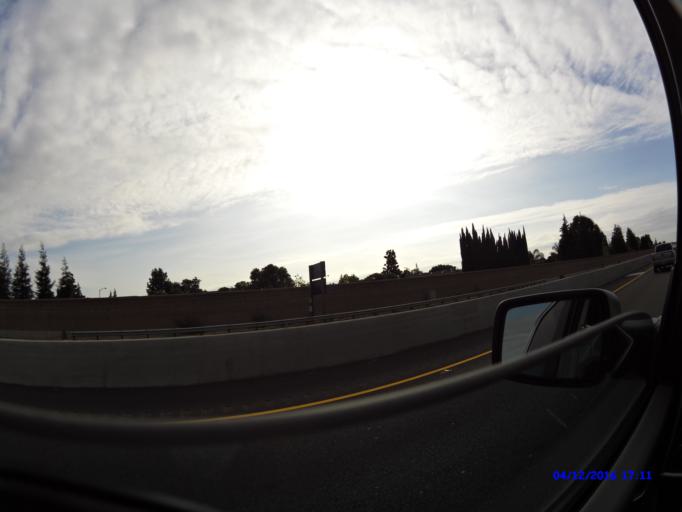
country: US
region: California
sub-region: San Joaquin County
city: Manteca
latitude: 37.8156
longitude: -121.2090
